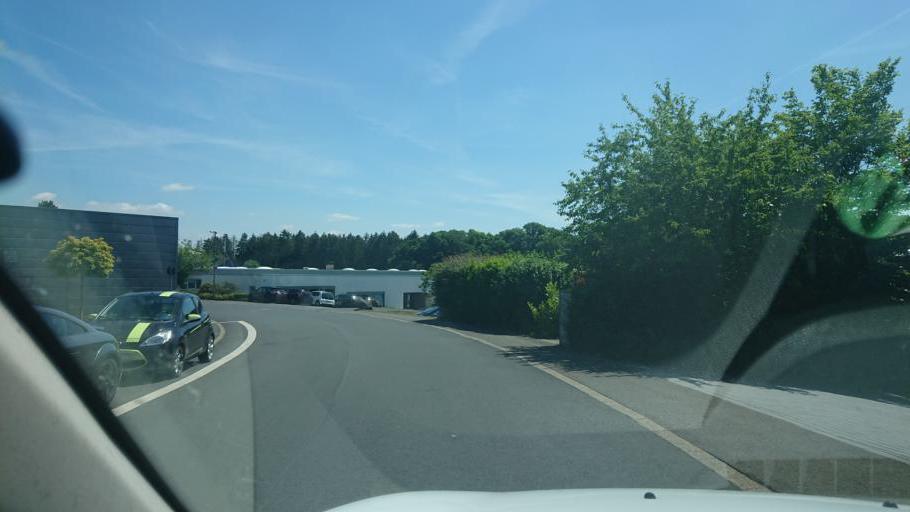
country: DE
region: North Rhine-Westphalia
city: Wermelskirchen
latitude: 51.1429
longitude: 7.2396
